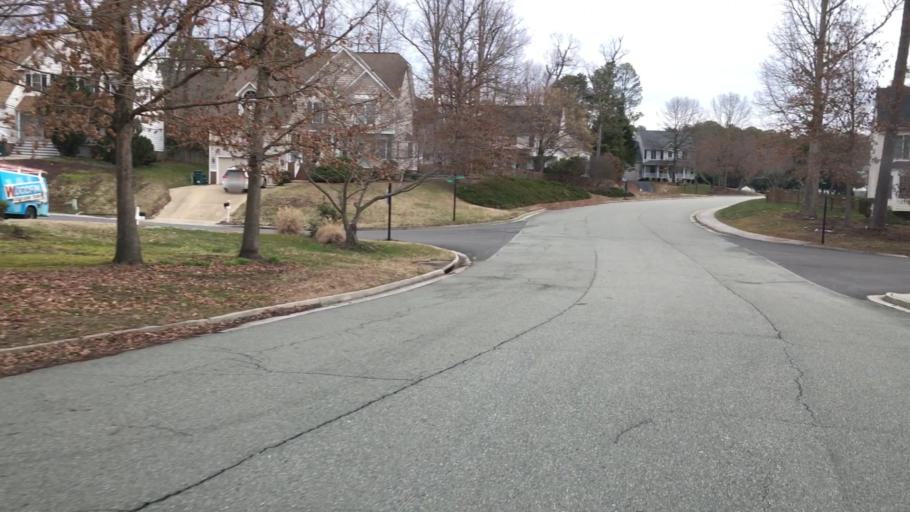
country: US
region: Virginia
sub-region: Henrico County
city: Short Pump
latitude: 37.6516
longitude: -77.5725
